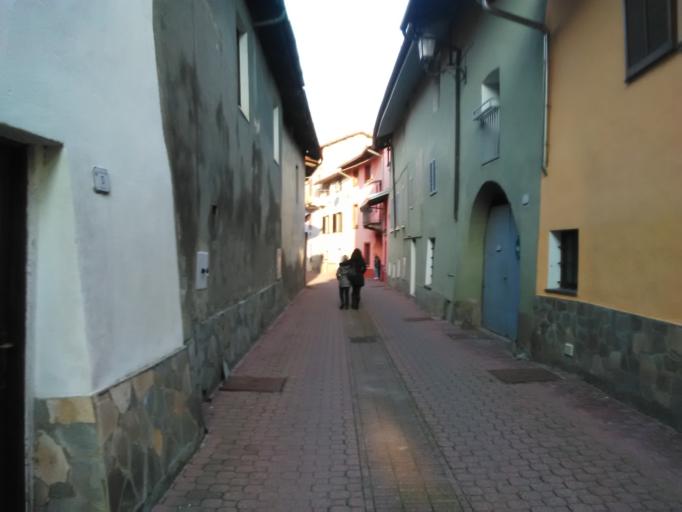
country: IT
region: Piedmont
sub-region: Provincia di Torino
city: Salerano Canavese
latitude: 45.4583
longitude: 7.8506
